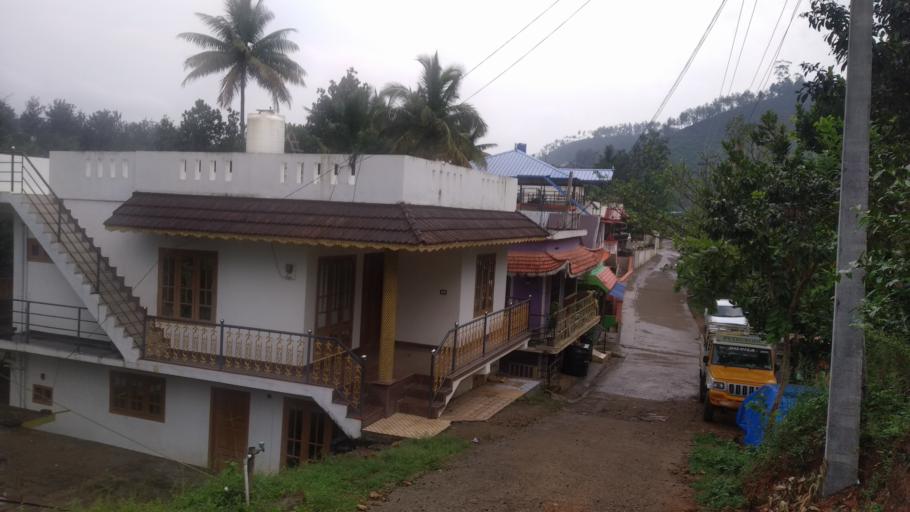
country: IN
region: Tamil Nadu
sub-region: Theni
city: Gudalur
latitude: 9.5679
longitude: 77.0884
